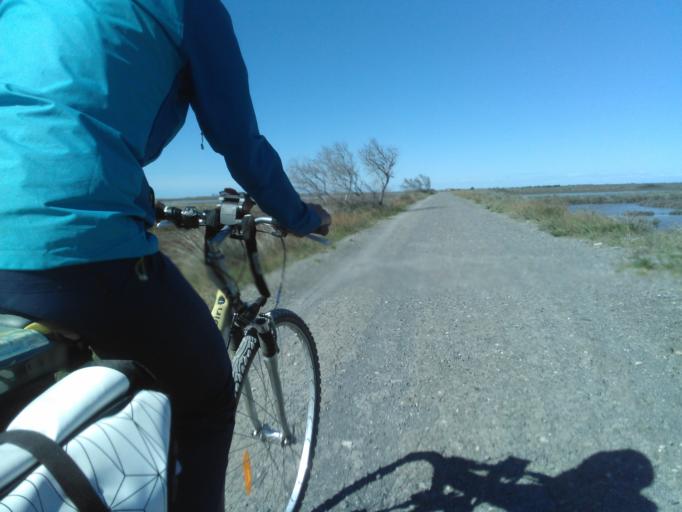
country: FR
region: Provence-Alpes-Cote d'Azur
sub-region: Departement des Bouches-du-Rhone
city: Saintes-Maries-de-la-Mer
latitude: 43.4548
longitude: 4.5679
